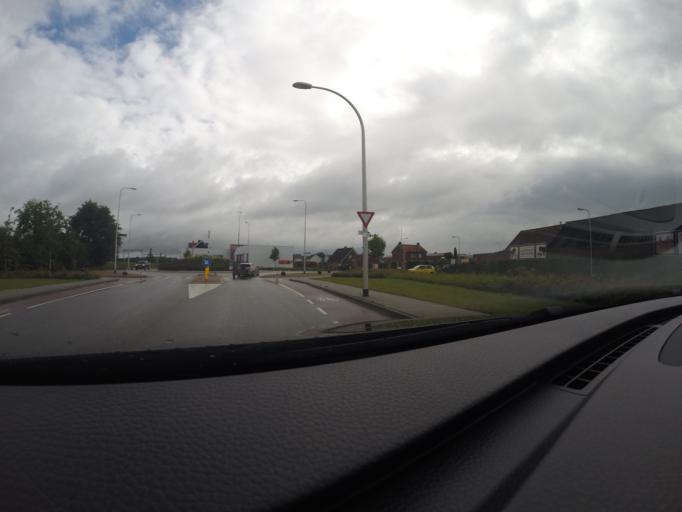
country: NL
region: Overijssel
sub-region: Gemeente Hof van Twente
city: Markelo
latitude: 52.2844
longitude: 6.4248
